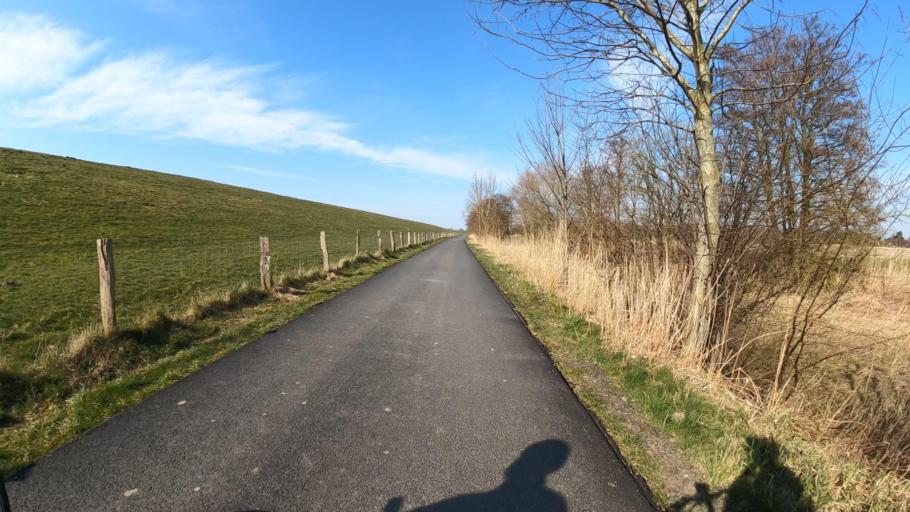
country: DE
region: Schleswig-Holstein
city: Haseldorf
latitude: 53.6395
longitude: 9.5695
